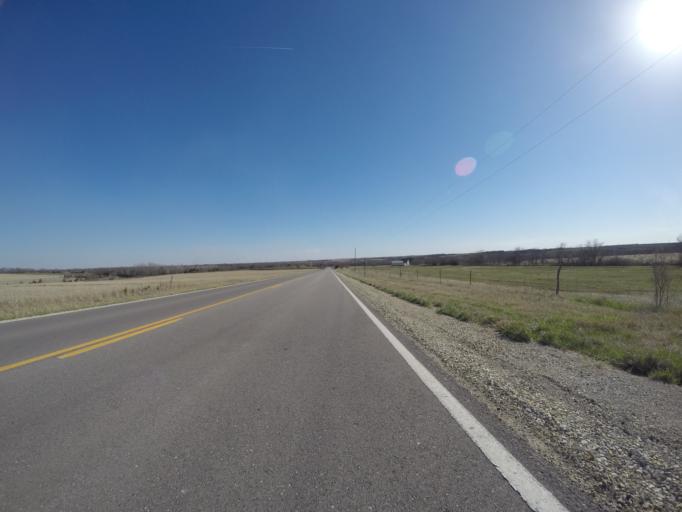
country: US
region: Kansas
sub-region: Riley County
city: Fort Riley North
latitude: 39.2676
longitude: -96.7753
